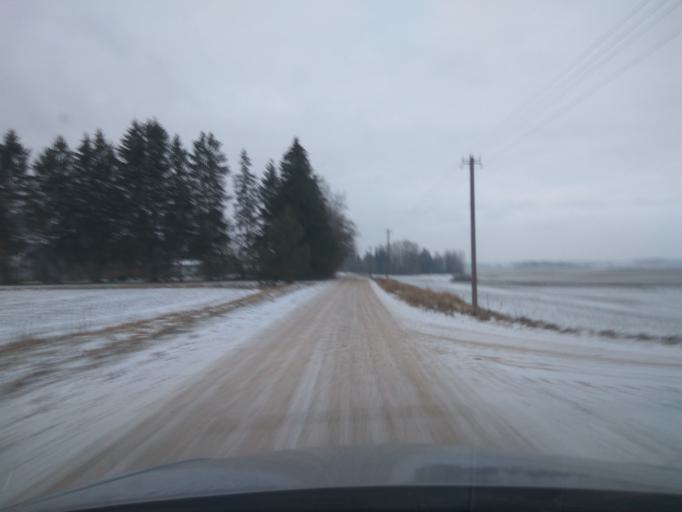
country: LV
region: Aizpute
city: Aizpute
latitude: 56.7587
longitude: 21.6993
